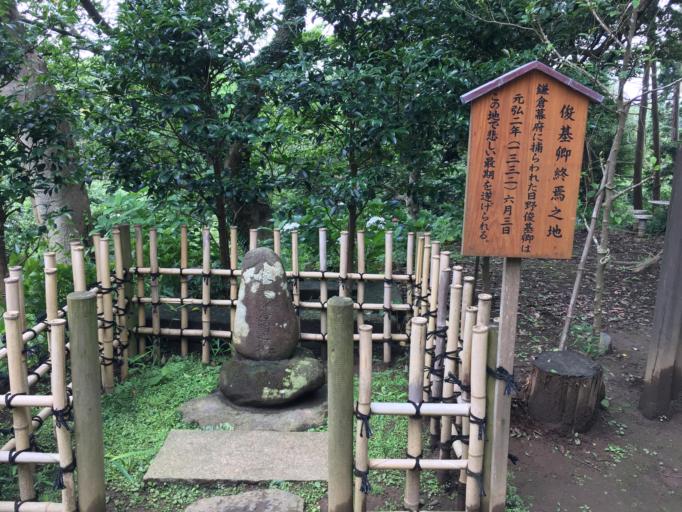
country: JP
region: Kanagawa
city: Kamakura
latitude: 35.3290
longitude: 139.5425
